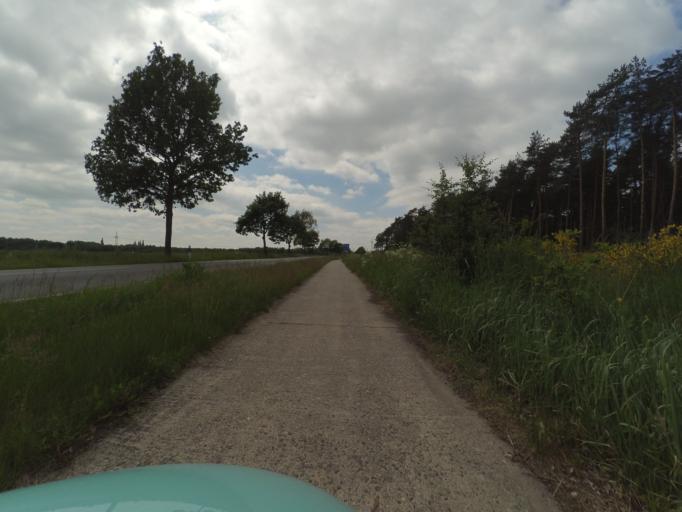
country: DE
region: Lower Saxony
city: Lehrte
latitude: 52.3859
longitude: 10.0255
